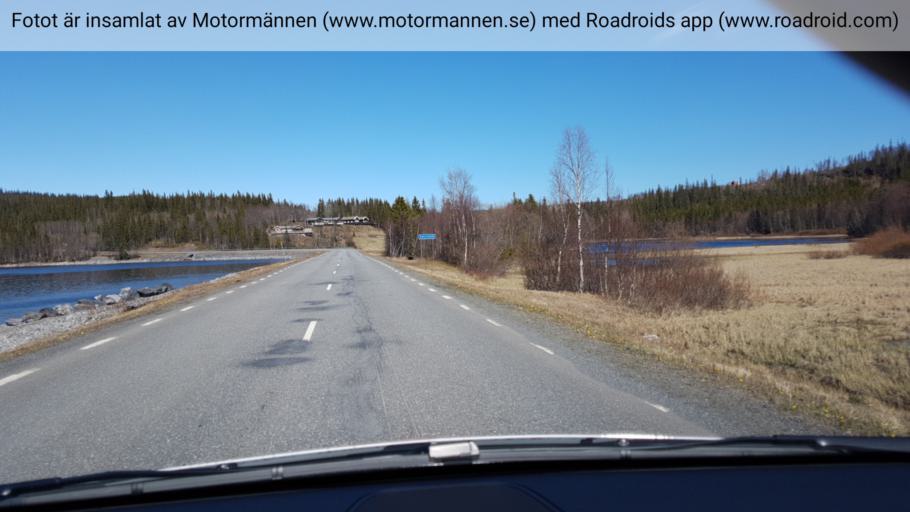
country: SE
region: Jaemtland
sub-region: Are Kommun
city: Are
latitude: 63.6106
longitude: 13.2016
